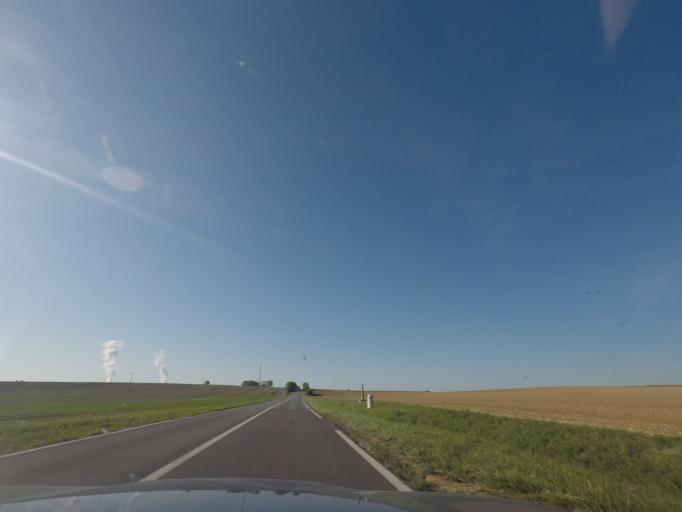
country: LU
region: Luxembourg
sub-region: Canton d'Esch-sur-Alzette
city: Frisange
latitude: 49.4862
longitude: 6.1911
